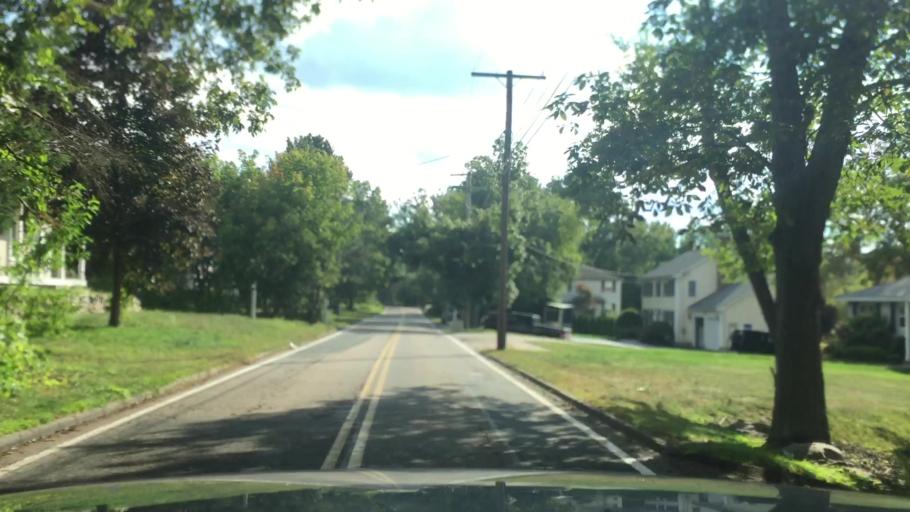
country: US
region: Massachusetts
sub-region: Norfolk County
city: Medway
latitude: 42.1543
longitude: -71.4241
